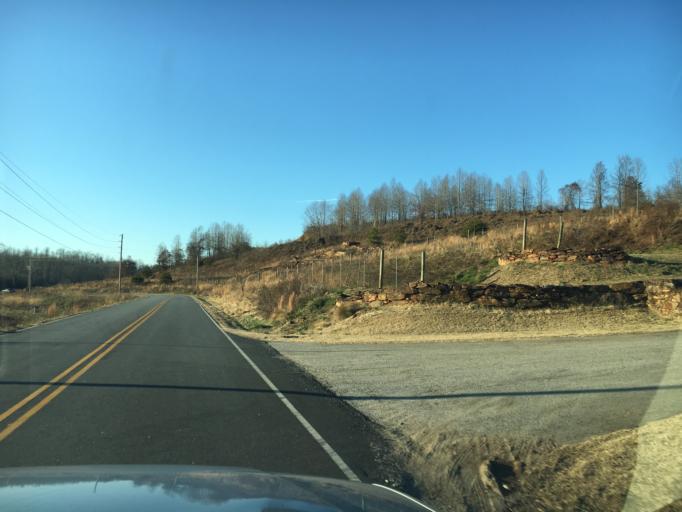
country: US
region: North Carolina
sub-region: Rutherford County
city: Rutherfordton
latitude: 35.2686
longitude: -82.0425
